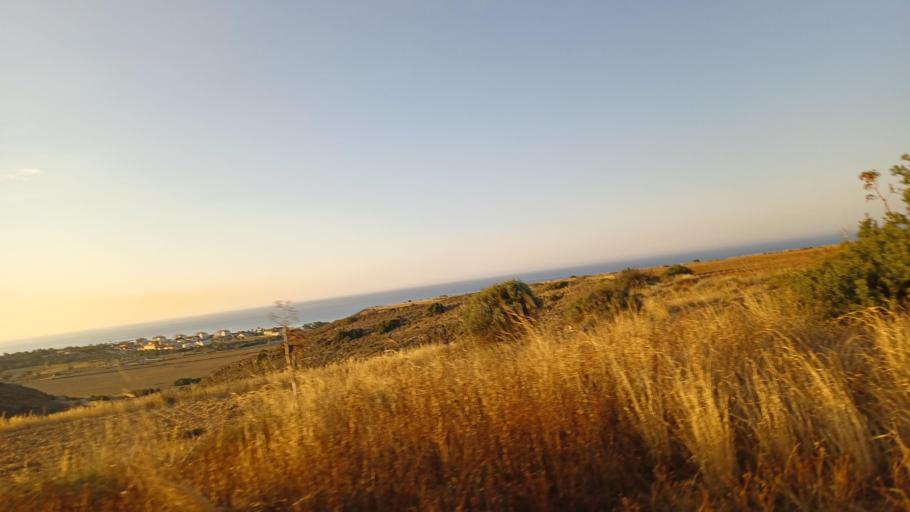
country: CY
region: Larnaka
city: Pyla
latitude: 34.9895
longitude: 33.7087
